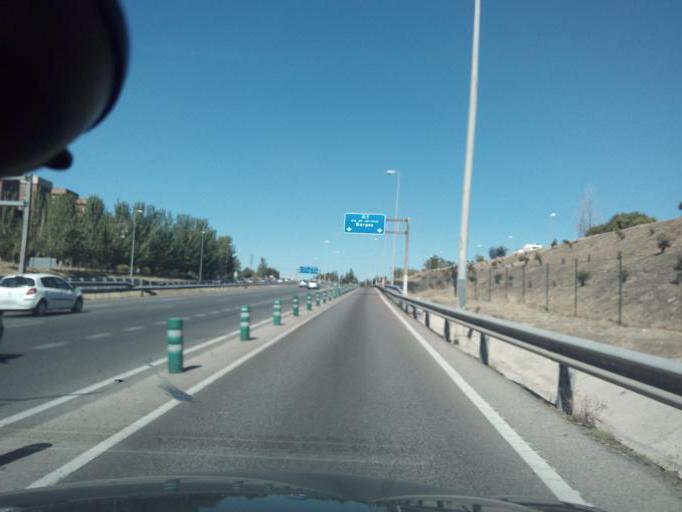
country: ES
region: Madrid
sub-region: Provincia de Madrid
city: Pinar de Chamartin
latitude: 40.4843
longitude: -3.6670
